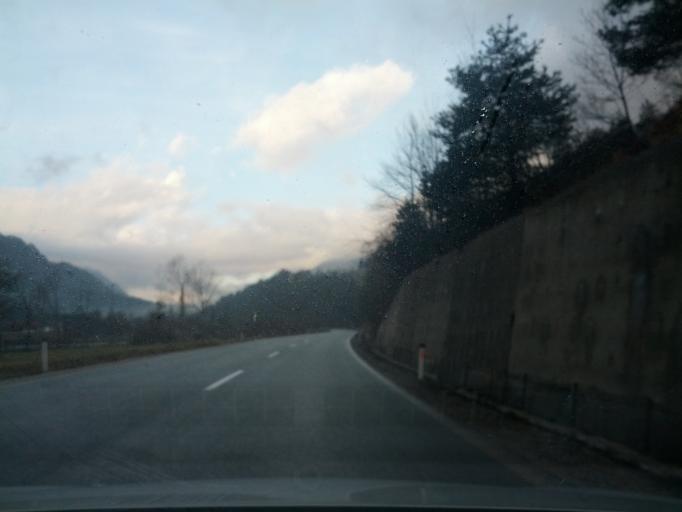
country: SI
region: Jesenice
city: Hrusica
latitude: 46.4495
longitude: 14.0045
